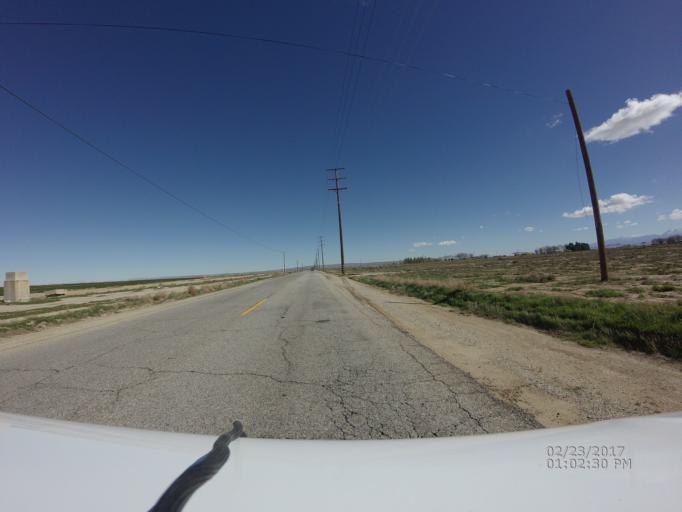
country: US
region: California
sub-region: Los Angeles County
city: Lancaster
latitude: 34.7634
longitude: -118.0103
